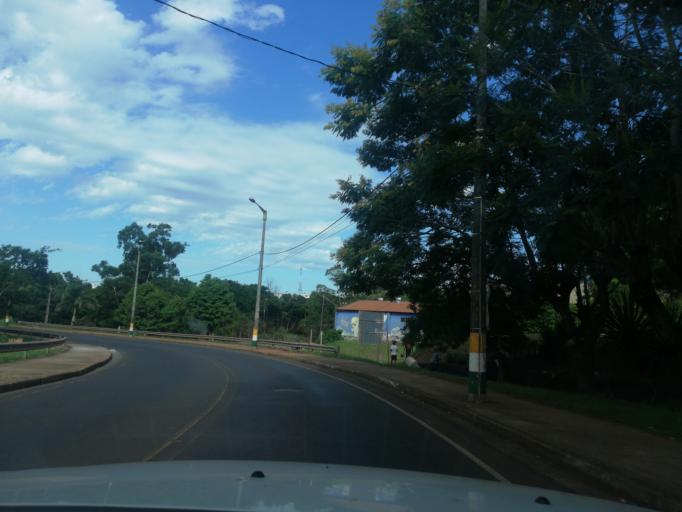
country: PY
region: Itapua
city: Encarnacion
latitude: -27.3423
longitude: -55.8514
